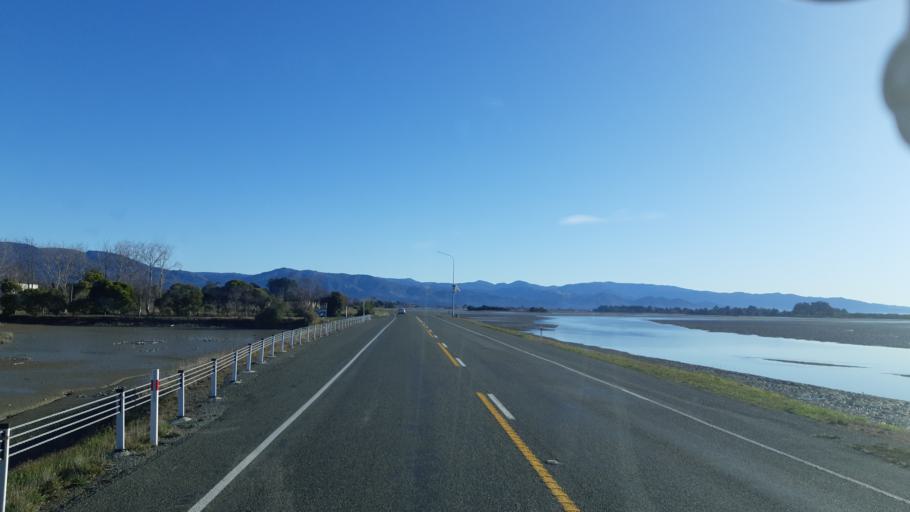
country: NZ
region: Tasman
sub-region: Tasman District
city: Motueka
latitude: -41.1779
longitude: 173.0423
